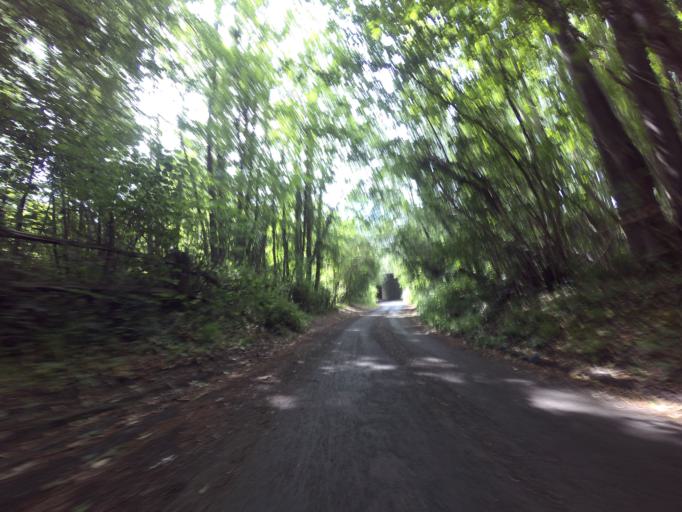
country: GB
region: England
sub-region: Kent
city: Halstead
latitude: 51.3468
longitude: 0.1433
